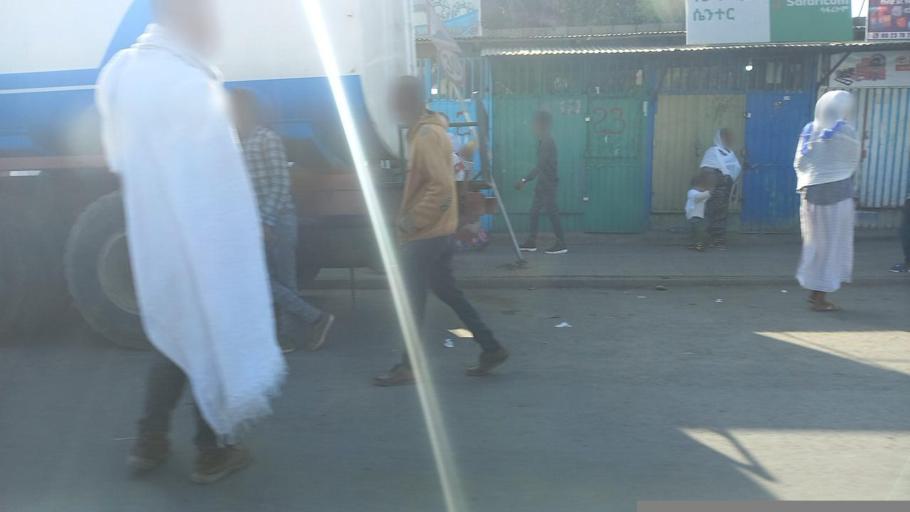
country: ET
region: Adis Abeba
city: Addis Ababa
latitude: 8.9404
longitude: 38.7499
